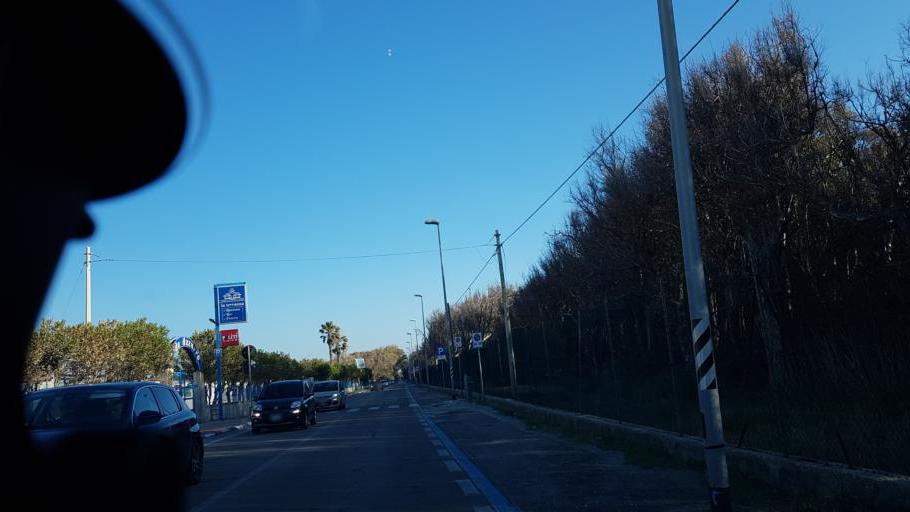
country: IT
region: Apulia
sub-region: Provincia di Lecce
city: Struda
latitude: 40.3791
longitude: 18.3092
